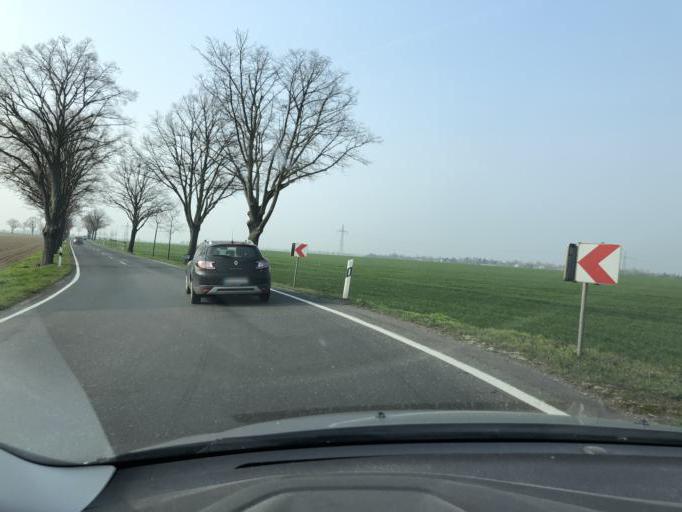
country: DE
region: Saxony-Anhalt
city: Roitzsch
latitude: 51.5378
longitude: 12.2751
